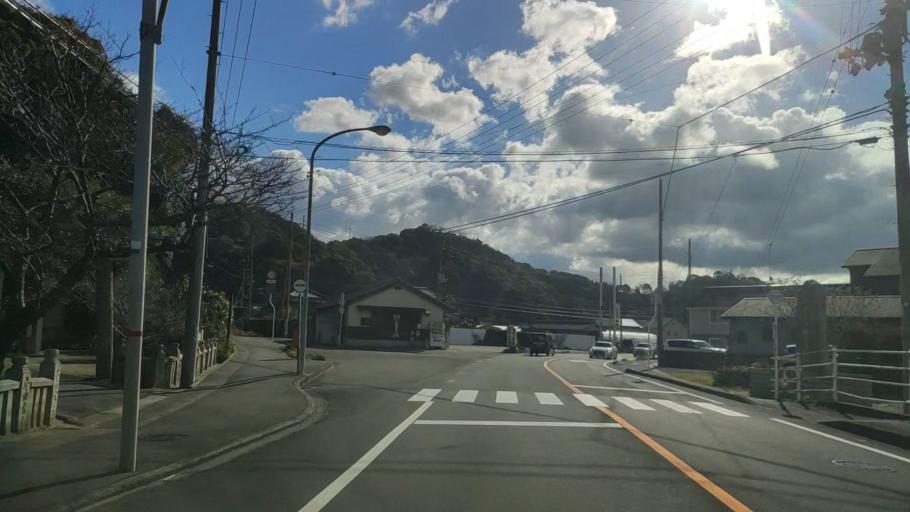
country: JP
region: Ehime
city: Masaki-cho
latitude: 33.8411
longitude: 132.7087
